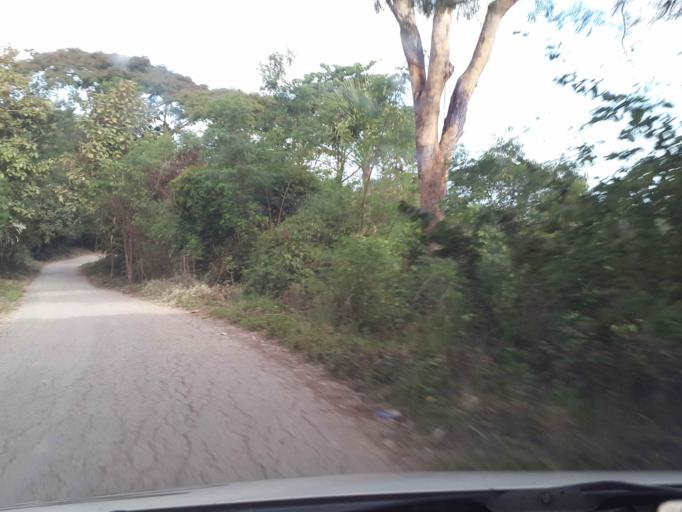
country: ID
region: East Nusa Tenggara
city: Biudukfoho
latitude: -9.5088
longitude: 124.9279
